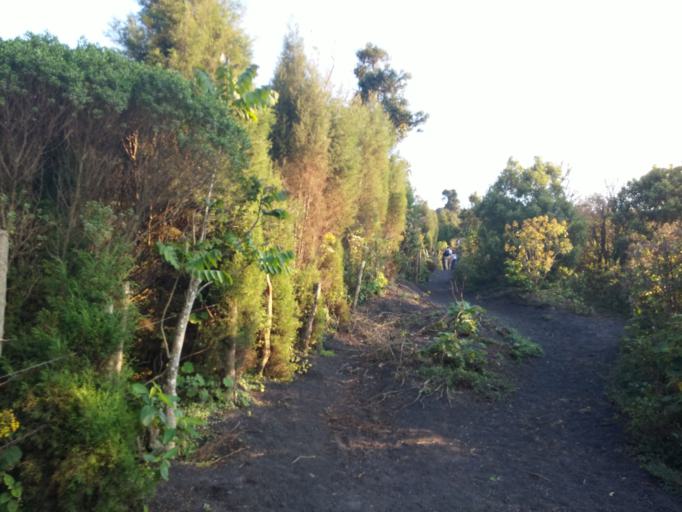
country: GT
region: Escuintla
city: San Vicente Pacaya
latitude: 14.3915
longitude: -90.5995
